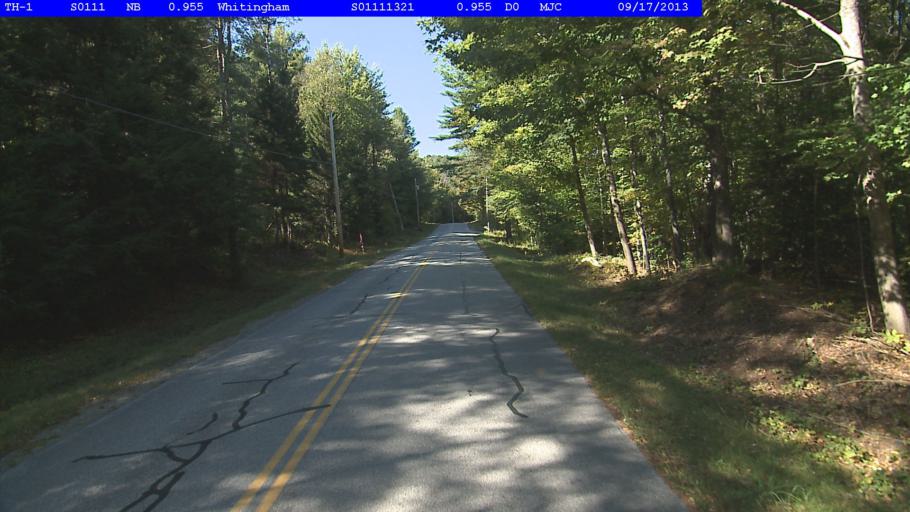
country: US
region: Massachusetts
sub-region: Franklin County
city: Charlemont
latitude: 42.7499
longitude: -72.8184
